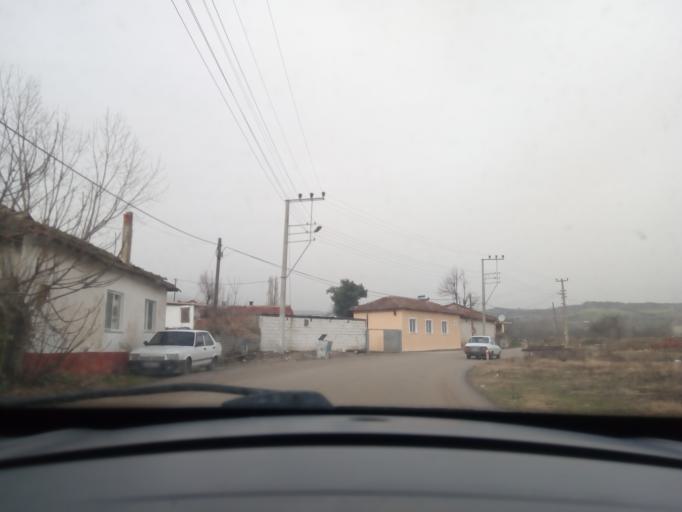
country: TR
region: Balikesir
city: Susurluk
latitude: 39.9208
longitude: 28.1467
